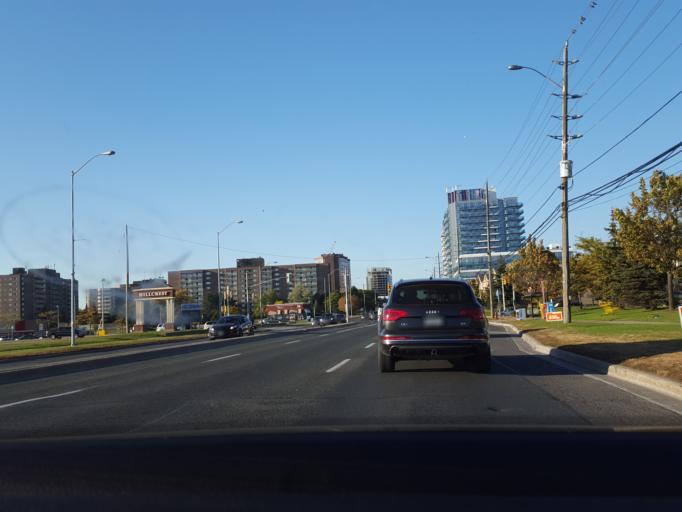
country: CA
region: Ontario
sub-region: York
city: Richmond Hill
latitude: 43.8546
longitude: -79.4333
